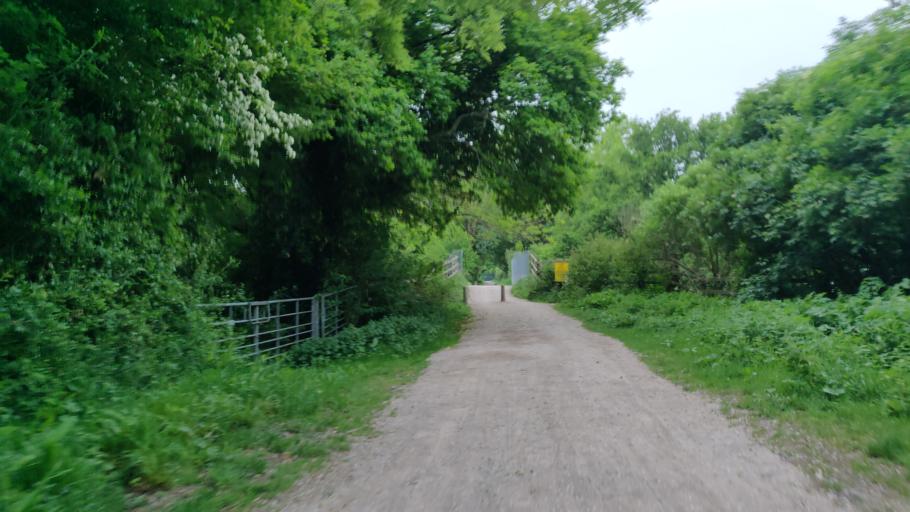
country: GB
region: England
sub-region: West Sussex
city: Partridge Green
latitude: 50.9738
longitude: -0.3159
